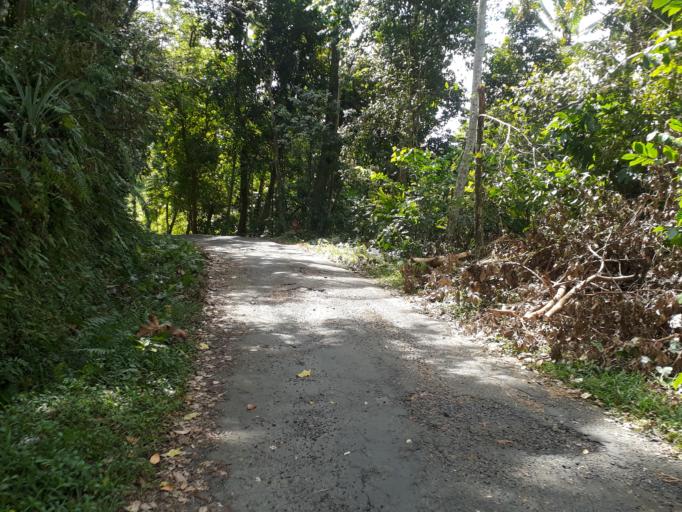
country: ID
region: Bali
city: Banjar Wangsian
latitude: -8.4598
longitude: 115.4353
